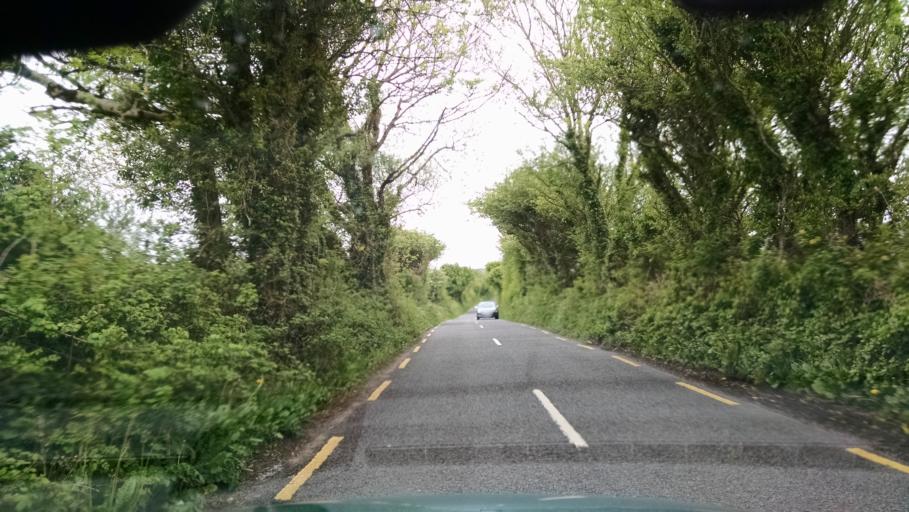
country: IE
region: Connaught
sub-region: County Galway
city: Bearna
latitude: 53.0887
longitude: -9.1593
